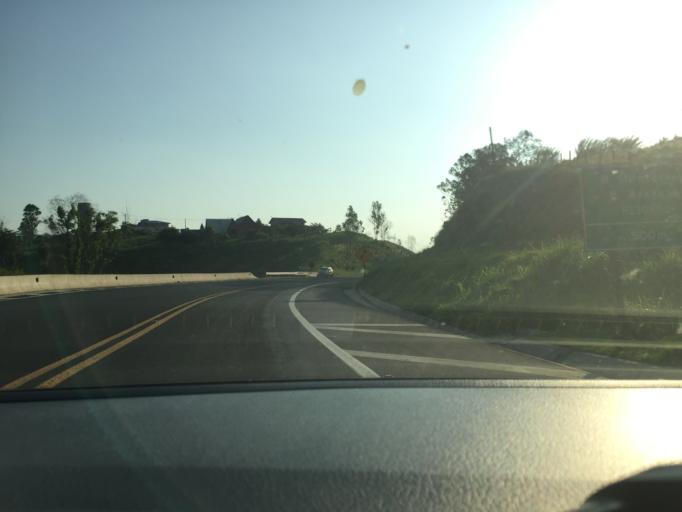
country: BR
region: Sao Paulo
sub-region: Louveira
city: Louveira
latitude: -23.0700
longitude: -46.9026
